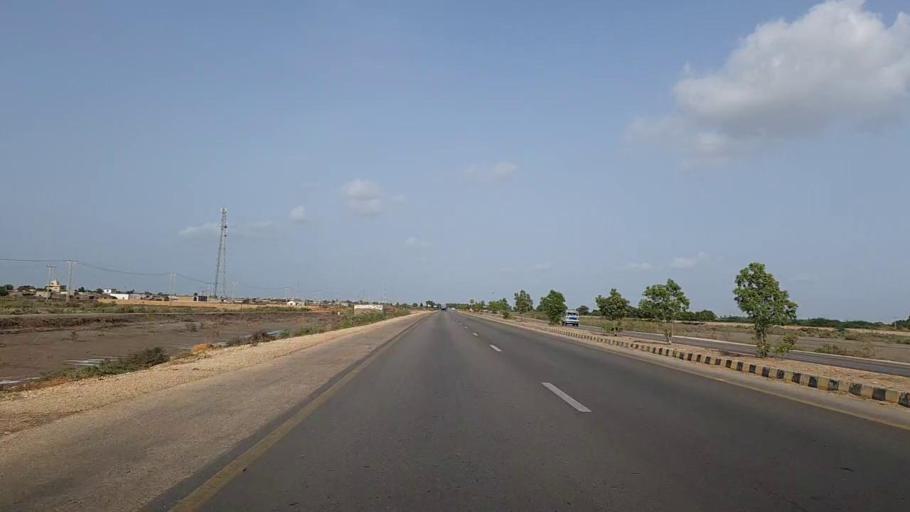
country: PK
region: Sindh
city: Gharo
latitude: 24.7397
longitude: 67.7504
